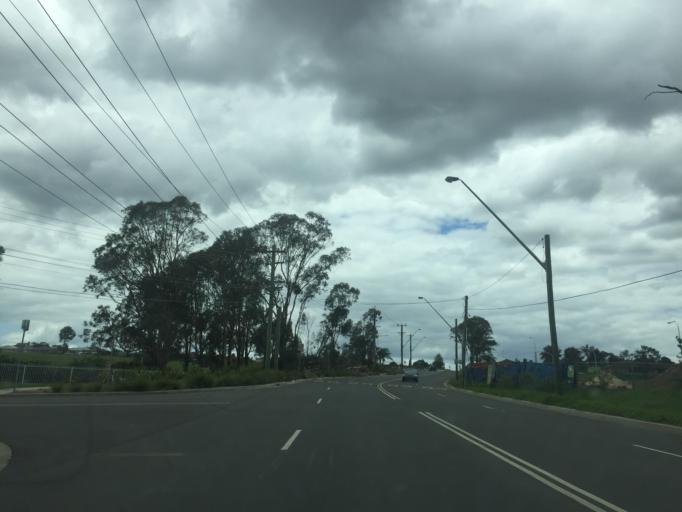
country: AU
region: New South Wales
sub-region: Blacktown
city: Quakers Hill
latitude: -33.7112
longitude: 150.8795
